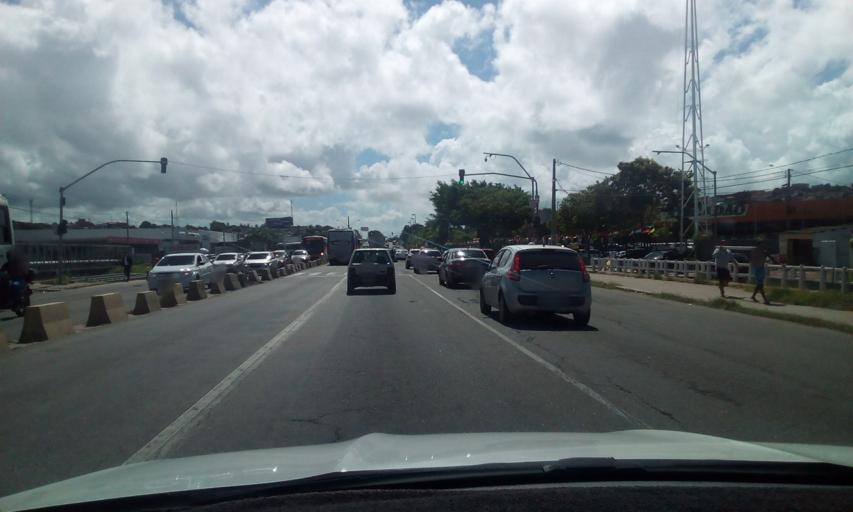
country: BR
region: Pernambuco
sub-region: Olinda
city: Olinda
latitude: -8.0127
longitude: -34.8592
